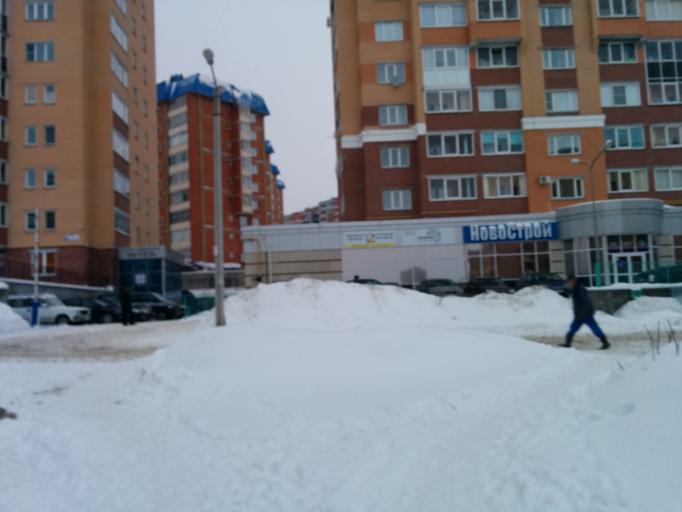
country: RU
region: Chuvashia
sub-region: Cheboksarskiy Rayon
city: Cheboksary
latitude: 56.1409
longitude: 47.2305
